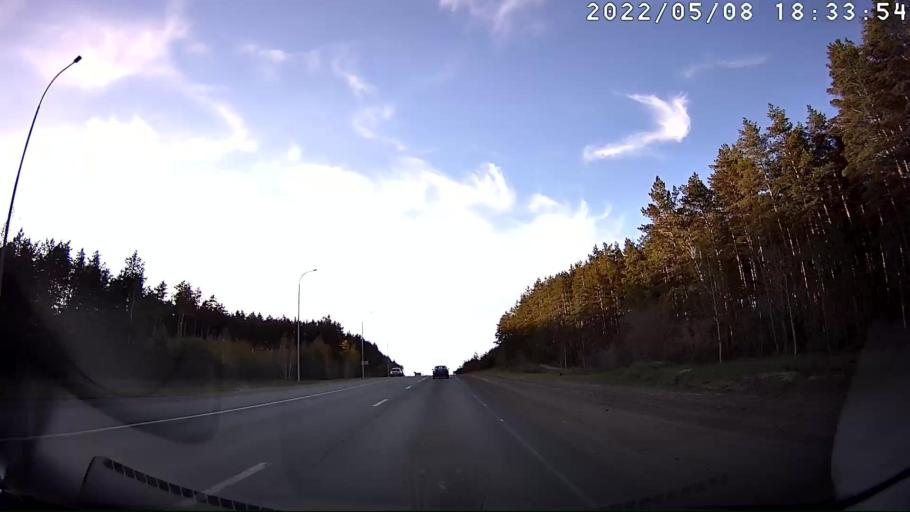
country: RU
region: Mariy-El
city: Volzhsk
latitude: 55.8949
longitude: 48.3566
